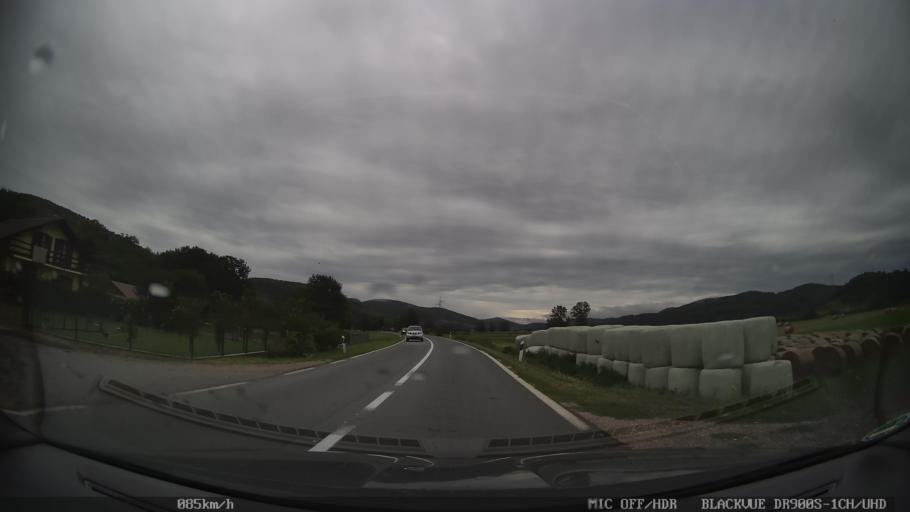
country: HR
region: Licko-Senjska
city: Brinje
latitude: 44.9202
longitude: 15.1459
